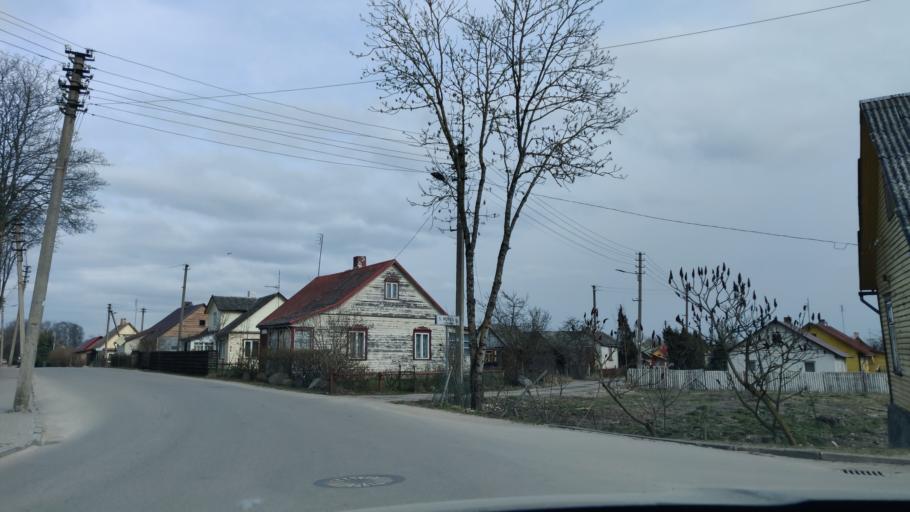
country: LT
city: Jieznas
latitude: 54.5994
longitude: 24.1753
